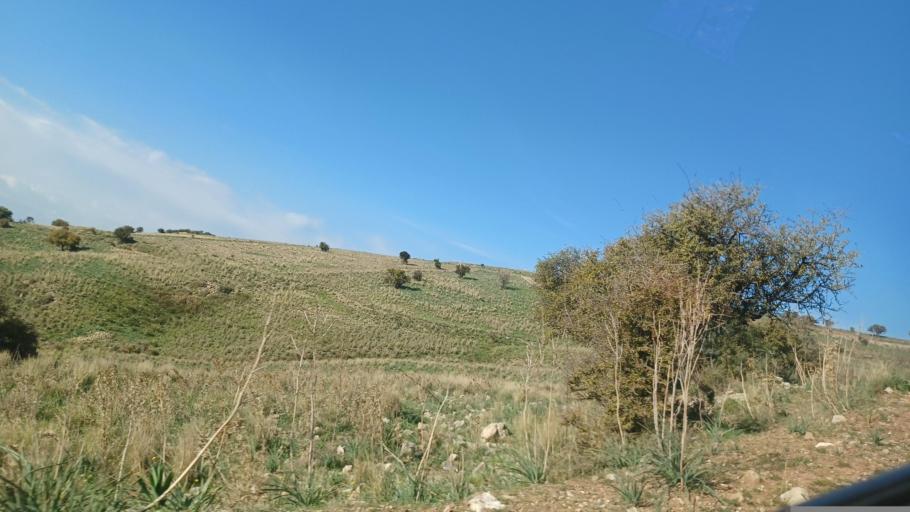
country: CY
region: Pafos
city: Mesogi
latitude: 34.7749
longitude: 32.5456
